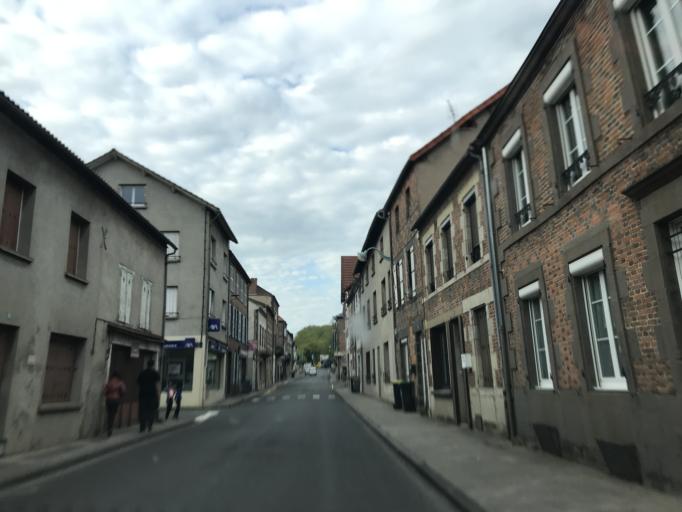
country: FR
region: Auvergne
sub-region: Departement du Puy-de-Dome
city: Randan
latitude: 46.0134
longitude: 3.3532
